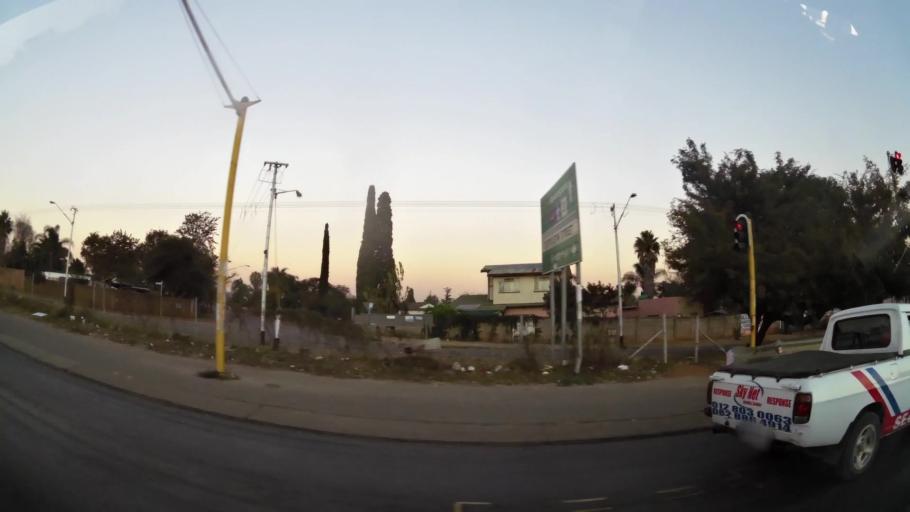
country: ZA
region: Gauteng
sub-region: City of Tshwane Metropolitan Municipality
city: Pretoria
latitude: -25.7310
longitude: 28.3181
